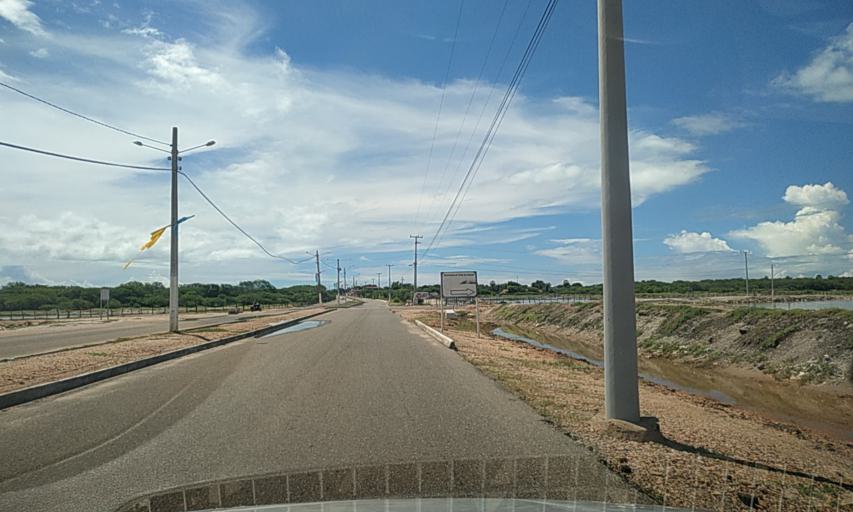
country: BR
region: Rio Grande do Norte
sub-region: Areia Branca
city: Areia Branca
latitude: -4.9360
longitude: -37.1134
